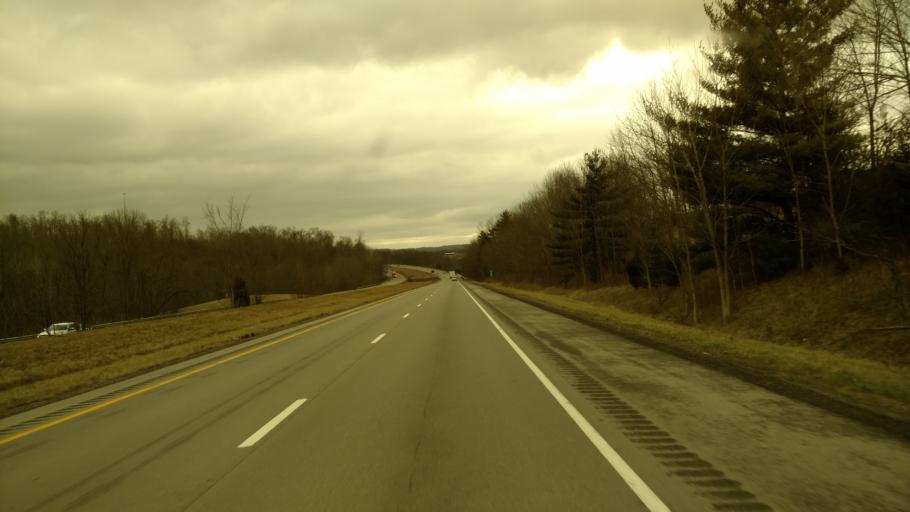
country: US
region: Ohio
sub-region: Muskingum County
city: Zanesville
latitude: 39.9526
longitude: -82.1835
